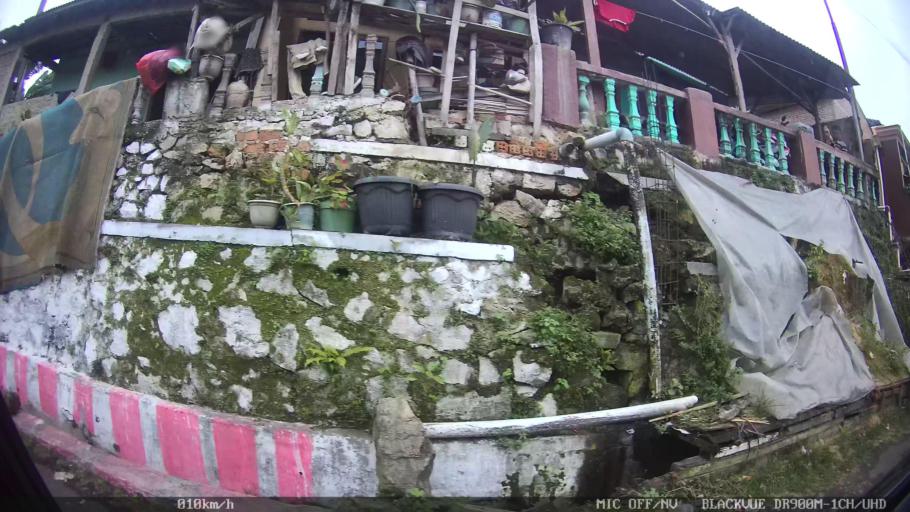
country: ID
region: Lampung
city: Bandarlampung
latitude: -5.4045
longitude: 105.2398
